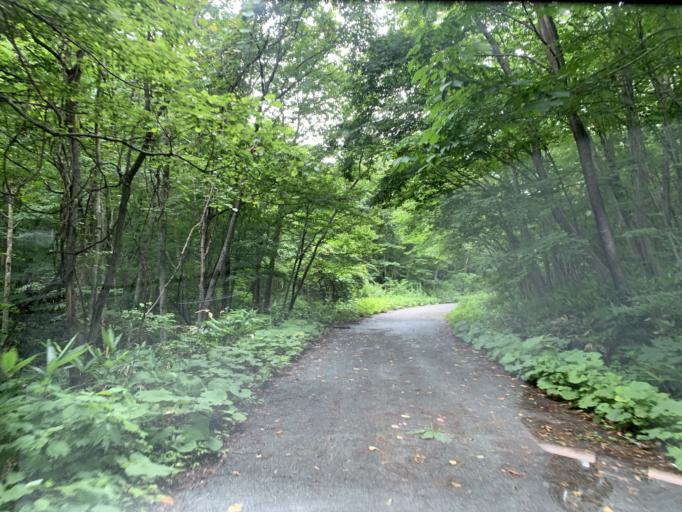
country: JP
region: Iwate
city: Ichinoseki
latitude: 38.9328
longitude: 140.8897
